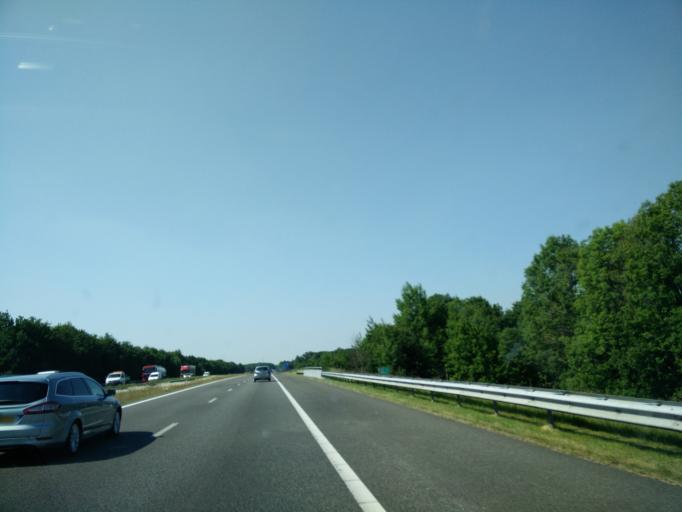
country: NL
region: Drenthe
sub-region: Gemeente Hoogeveen
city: Hoogeveen
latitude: 52.7612
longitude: 6.4525
